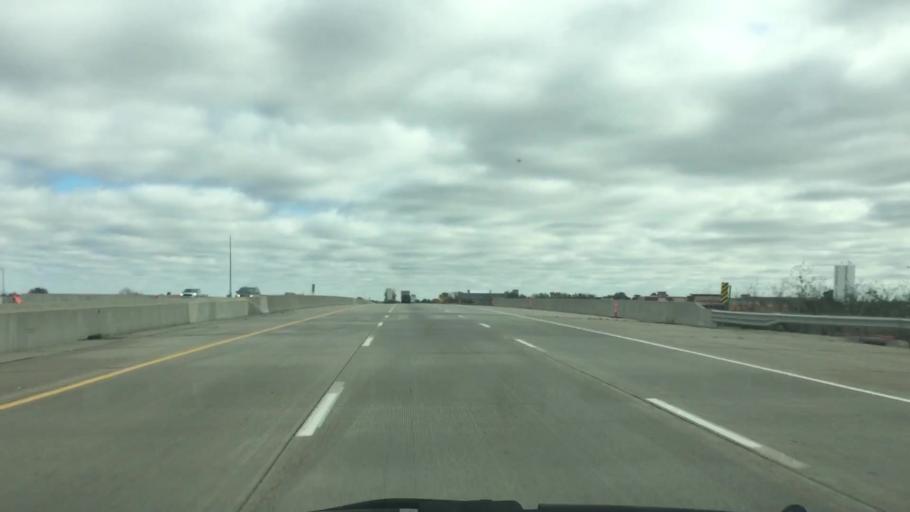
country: US
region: Iowa
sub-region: Polk County
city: Altoona
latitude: 41.6619
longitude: -93.4957
